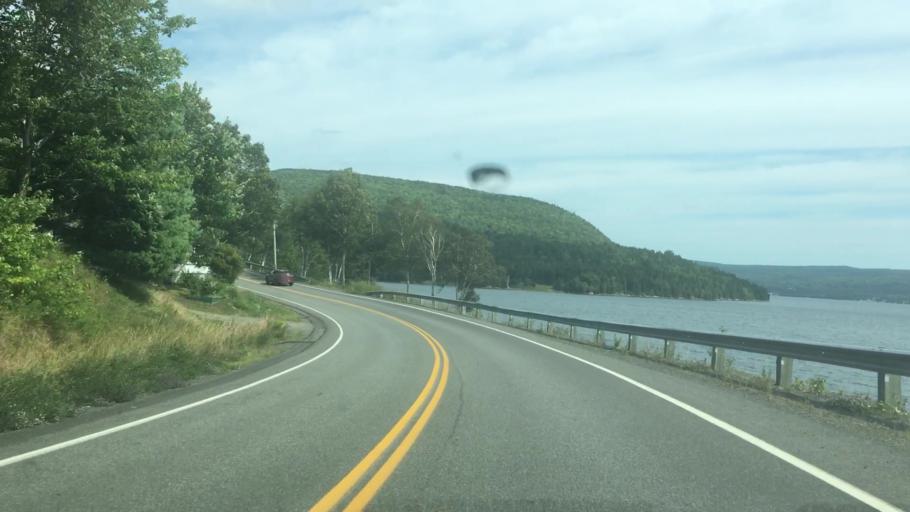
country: CA
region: Nova Scotia
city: Sydney Mines
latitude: 46.2659
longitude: -60.6098
